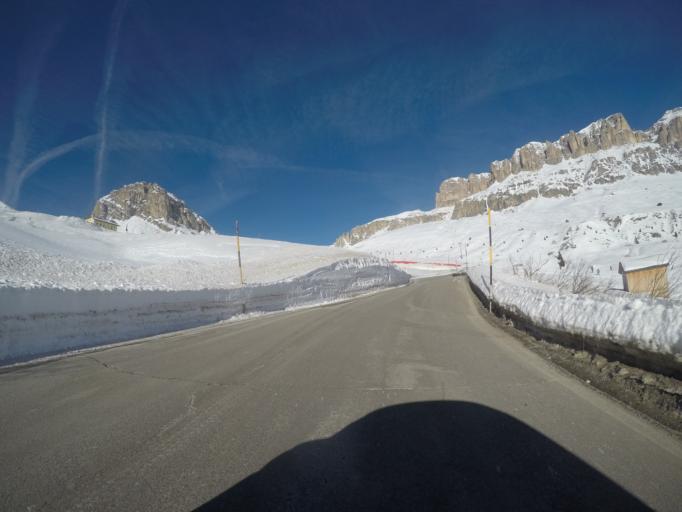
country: IT
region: Trentino-Alto Adige
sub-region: Provincia di Trento
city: Canazei
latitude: 46.4831
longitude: 11.8257
